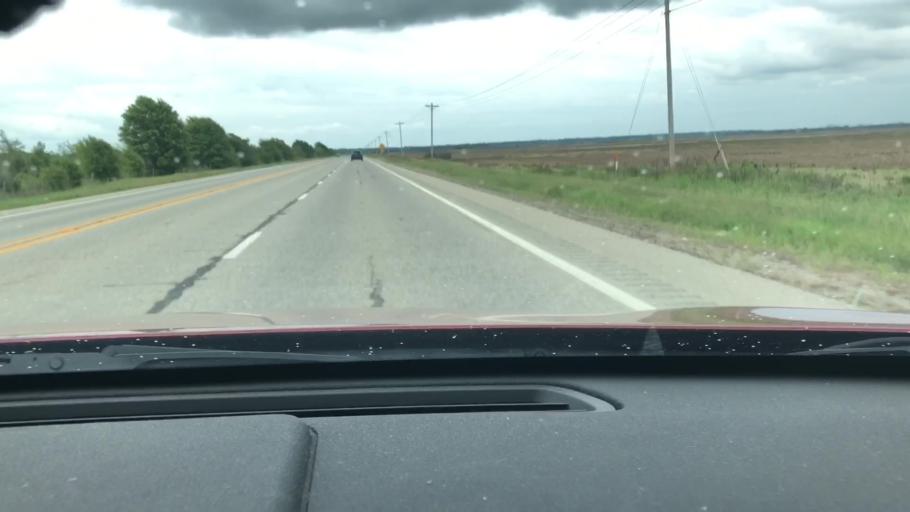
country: US
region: Arkansas
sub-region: Lafayette County
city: Lewisville
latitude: 33.4121
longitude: -93.7824
